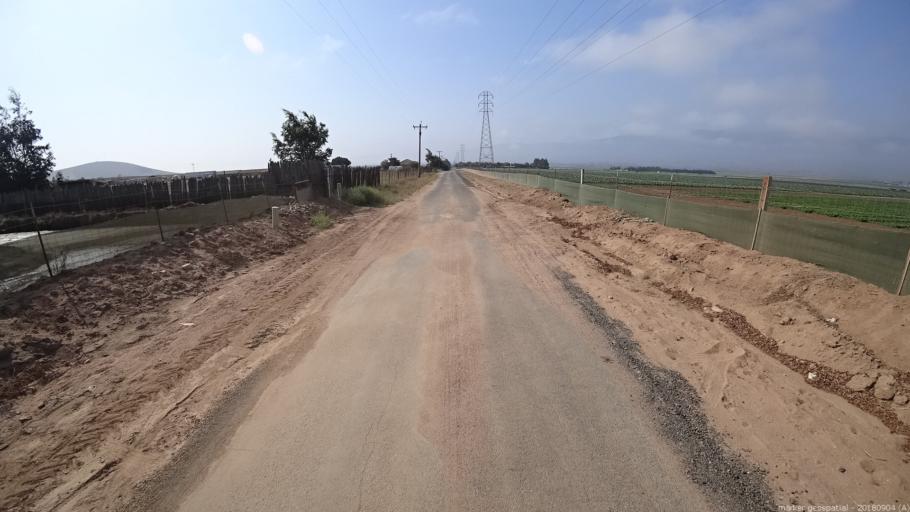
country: US
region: California
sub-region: Monterey County
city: Soledad
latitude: 36.4617
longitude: -121.3317
